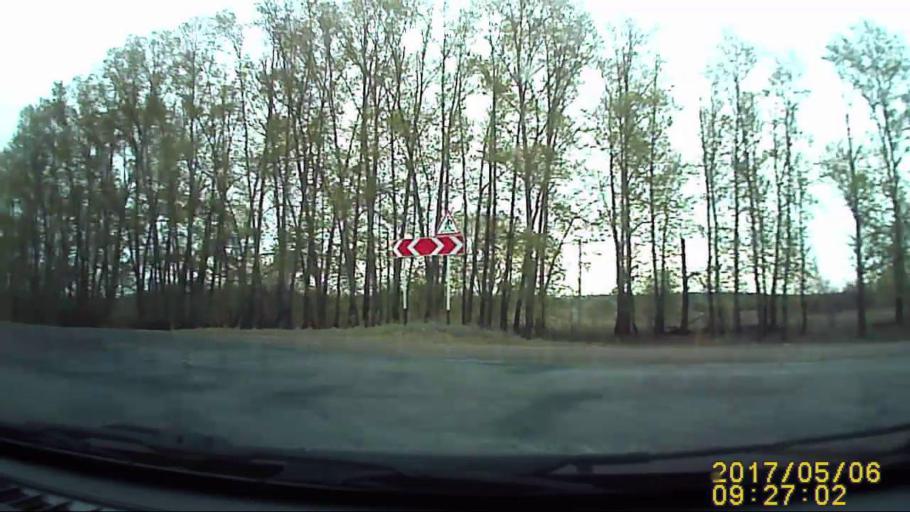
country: RU
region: Ulyanovsk
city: Cherdakly
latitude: 54.3856
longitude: 48.8427
